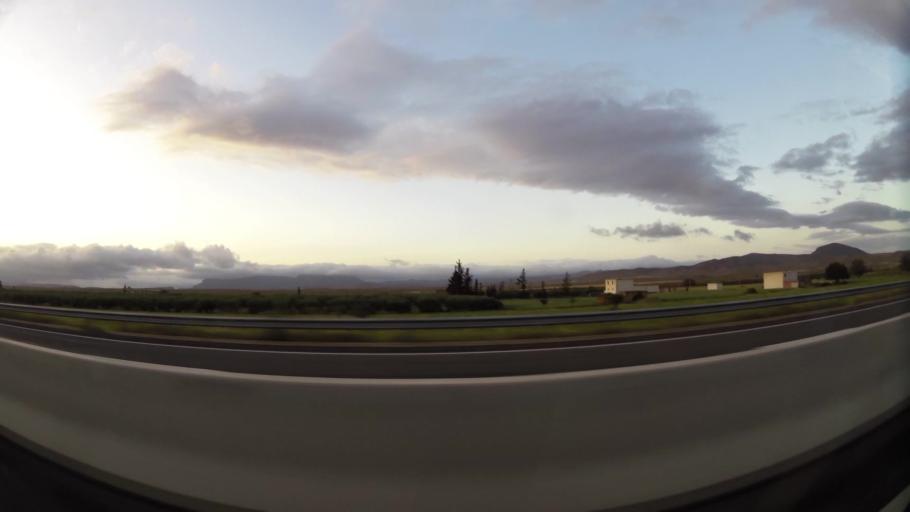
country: MA
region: Oriental
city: El Aioun
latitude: 34.5956
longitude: -2.7087
